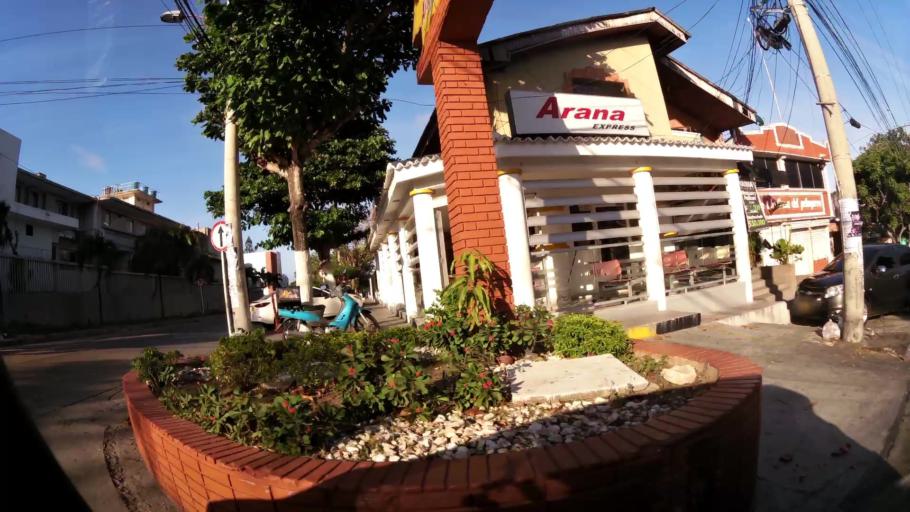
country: CO
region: Atlantico
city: Barranquilla
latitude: 10.9849
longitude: -74.8089
